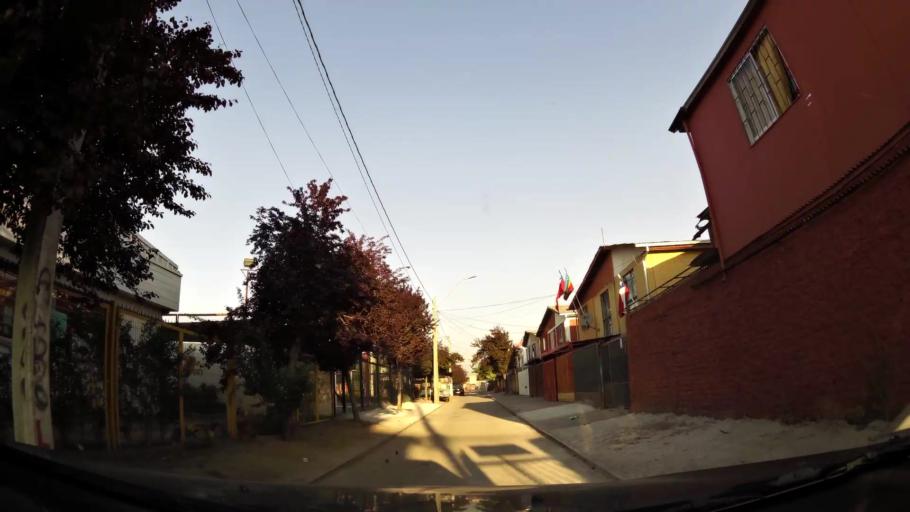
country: CL
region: Santiago Metropolitan
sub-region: Provincia de Maipo
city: San Bernardo
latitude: -33.5960
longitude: -70.6735
